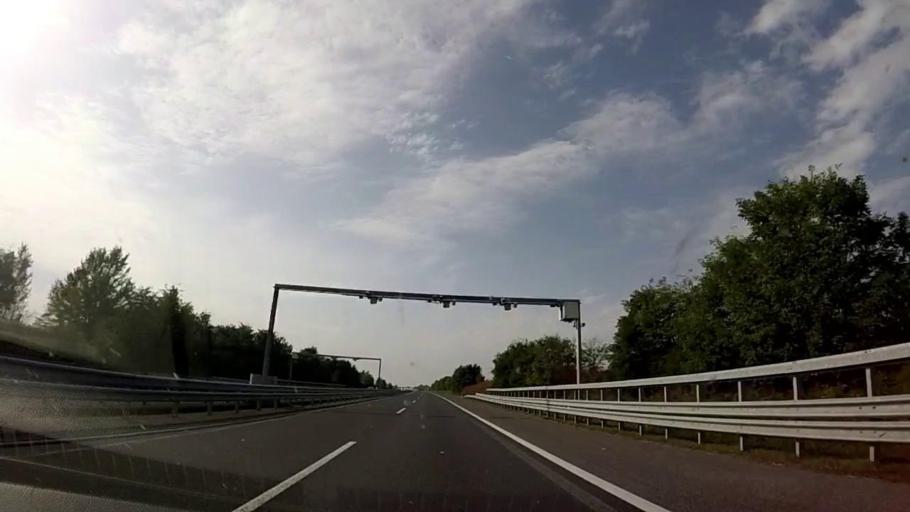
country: HU
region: Zala
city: Becsehely
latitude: 46.4420
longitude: 16.8111
